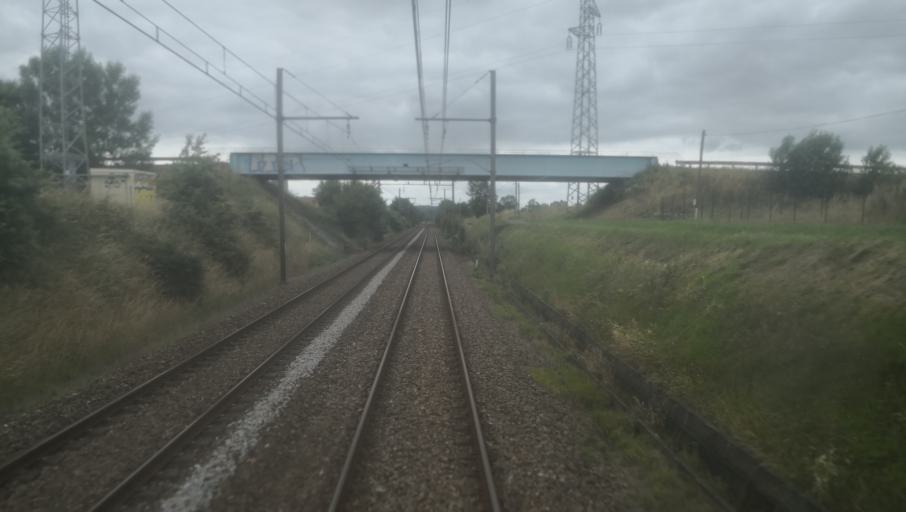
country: FR
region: Midi-Pyrenees
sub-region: Departement du Tarn-et-Garonne
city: Castelsarrasin
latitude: 44.0639
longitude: 1.1055
